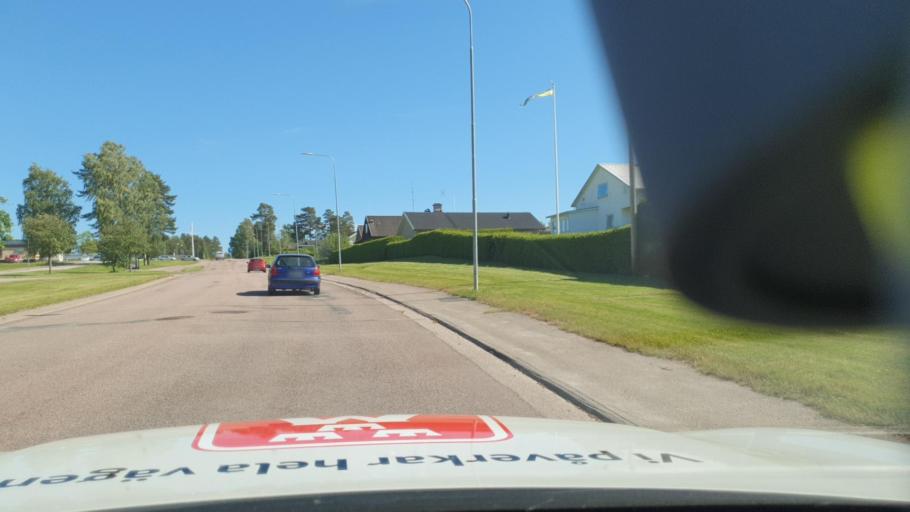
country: SE
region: Vaermland
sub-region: Kristinehamns Kommun
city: Kristinehamn
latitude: 59.3015
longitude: 14.0903
